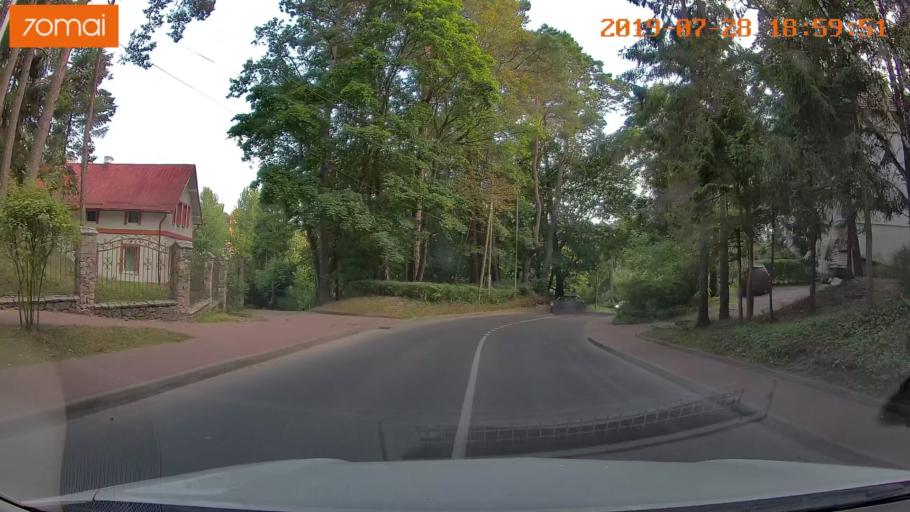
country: RU
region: Kaliningrad
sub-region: Gorod Svetlogorsk
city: Svetlogorsk
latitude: 54.9405
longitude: 20.1617
